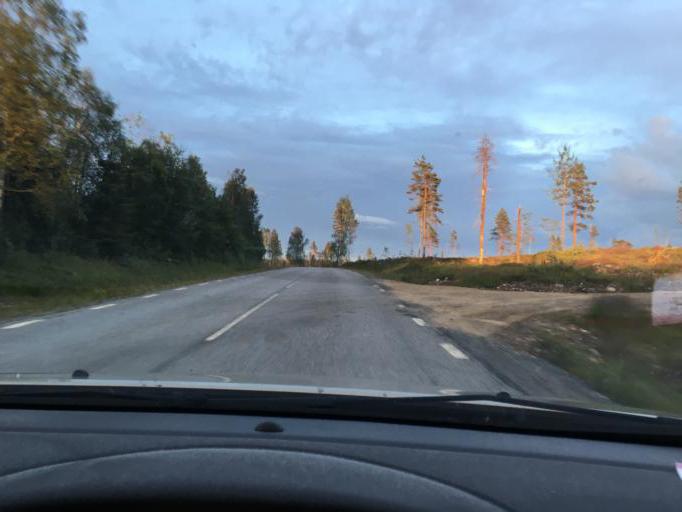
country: SE
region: Norrbotten
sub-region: Lulea Kommun
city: Ranea
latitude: 66.0501
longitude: 22.3930
